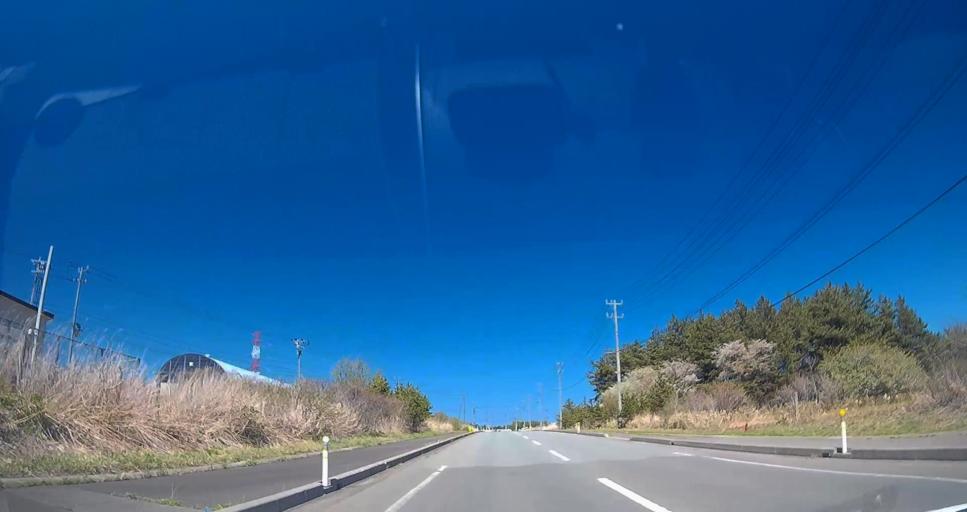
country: JP
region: Hokkaido
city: Hakodate
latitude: 41.5069
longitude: 140.9166
